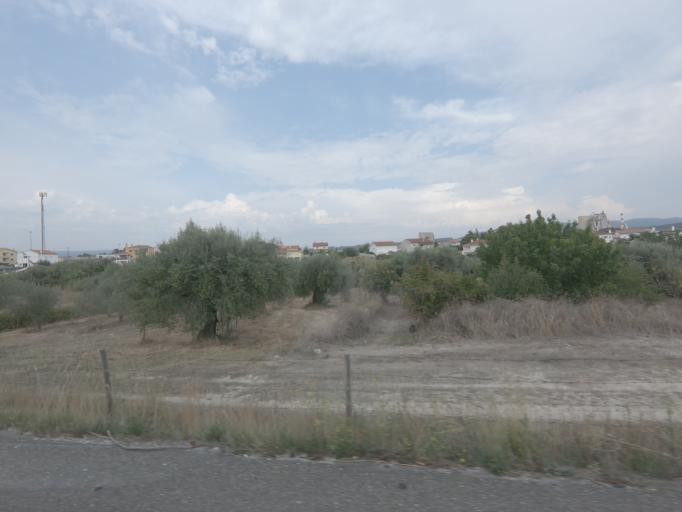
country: PT
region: Aveiro
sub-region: Mealhada
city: Pampilhosa do Botao
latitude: 40.2921
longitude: -8.4301
